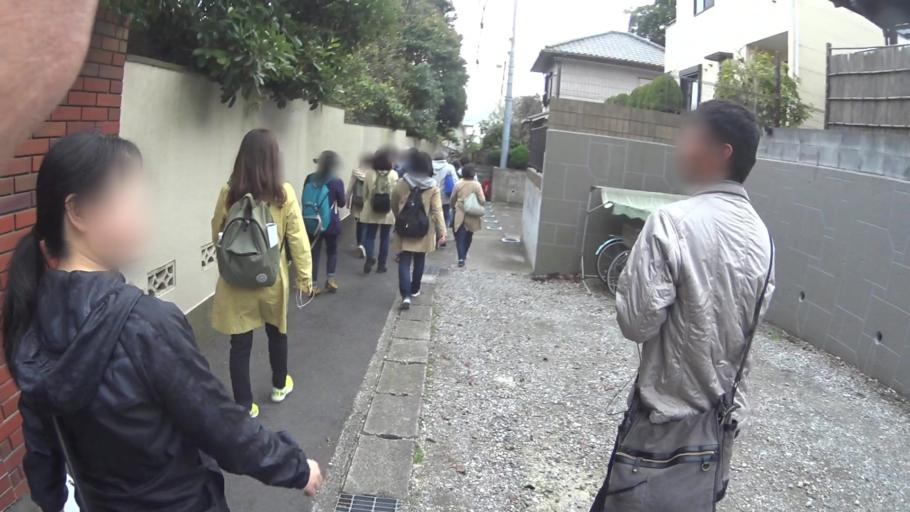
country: JP
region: Kanagawa
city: Fujisawa
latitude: 35.3116
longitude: 139.4918
